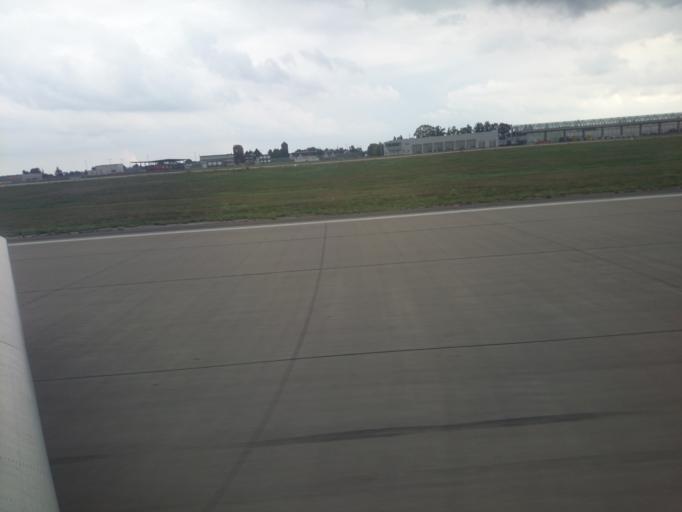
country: DE
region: Saxony
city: Schkeuditz
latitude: 51.4124
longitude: 12.2207
